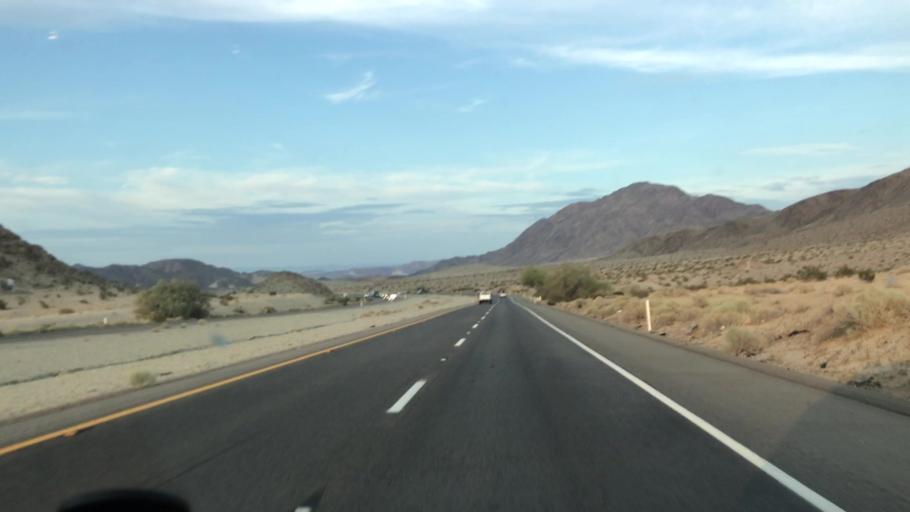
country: US
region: California
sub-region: San Bernardino County
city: Fort Irwin
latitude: 35.0791
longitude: -116.3923
